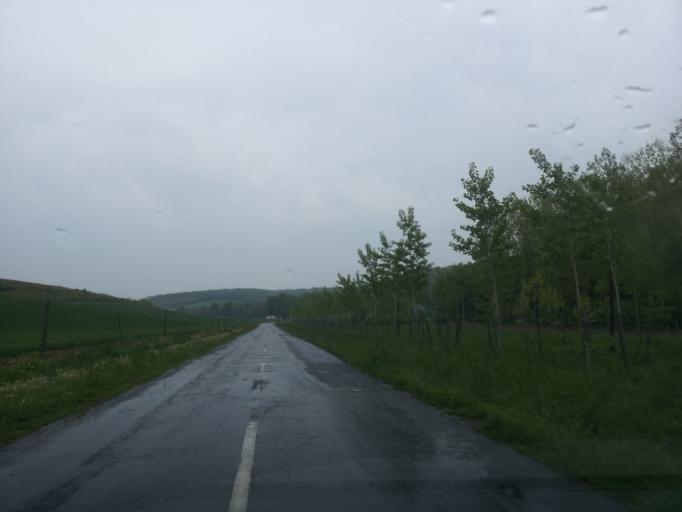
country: HU
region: Tolna
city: Szekszard
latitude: 46.2852
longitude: 18.6539
